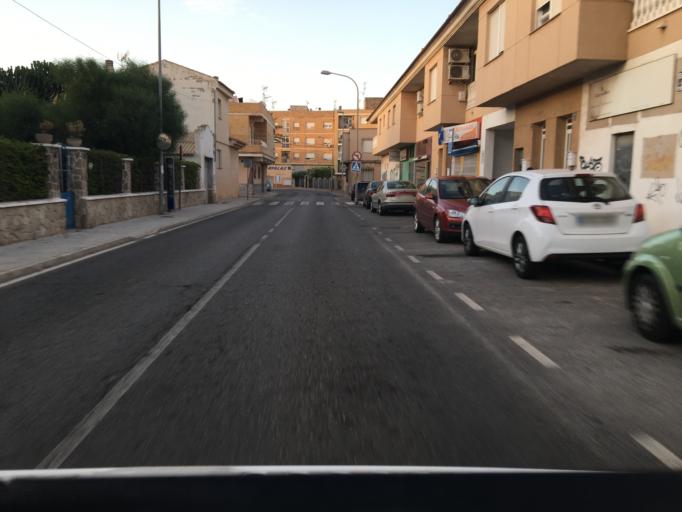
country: ES
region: Murcia
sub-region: Murcia
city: Cartagena
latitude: 37.6305
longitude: -0.9930
